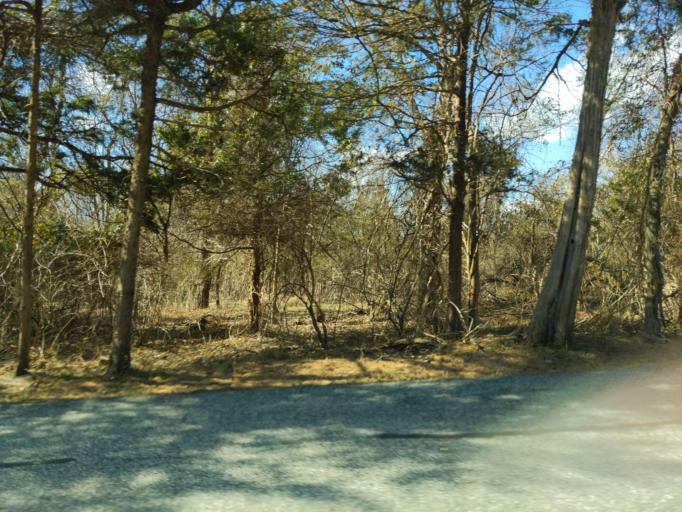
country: US
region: Pennsylvania
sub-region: Montgomery County
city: Red Hill
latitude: 40.3578
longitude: -75.4582
